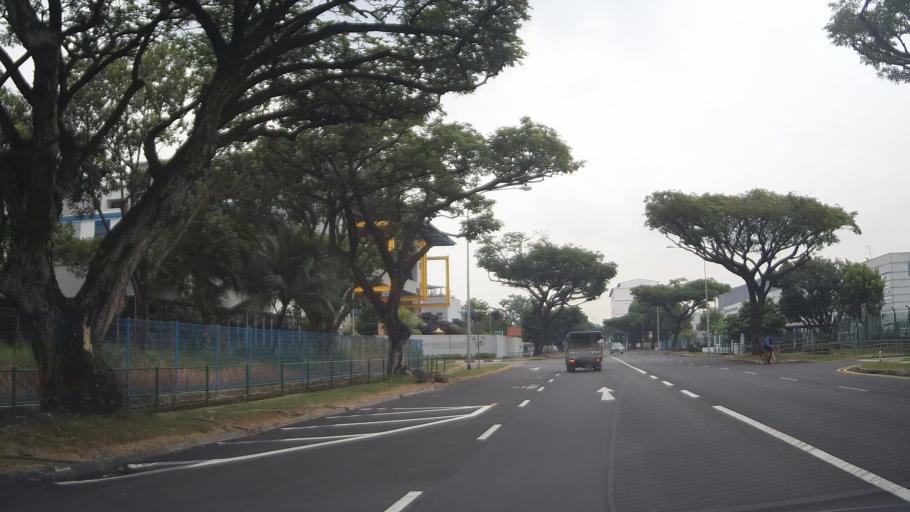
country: MY
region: Johor
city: Johor Bahru
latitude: 1.3155
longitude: 103.6627
